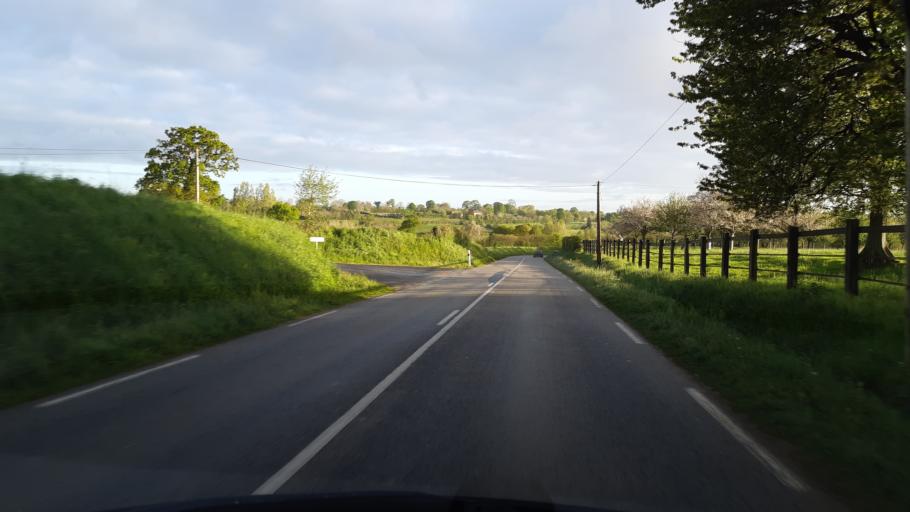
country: FR
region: Lower Normandy
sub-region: Departement de la Manche
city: Agneaux
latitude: 49.0642
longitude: -1.1326
